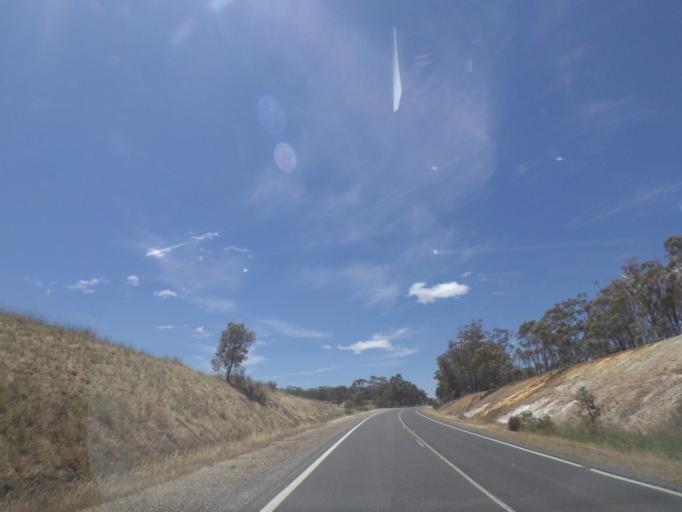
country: AU
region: Victoria
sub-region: Mount Alexander
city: Castlemaine
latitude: -37.1663
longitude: 144.1486
